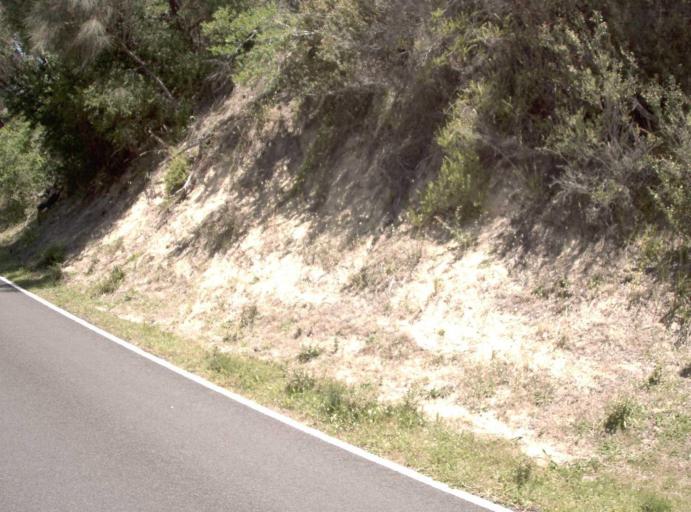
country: AU
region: Victoria
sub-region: Latrobe
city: Morwell
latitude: -38.8769
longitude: 146.2665
